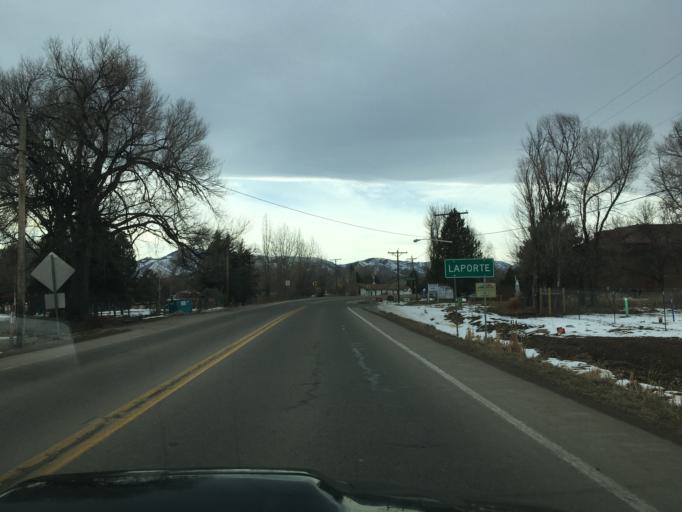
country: US
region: Colorado
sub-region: Larimer County
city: Laporte
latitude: 40.6257
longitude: -105.1325
